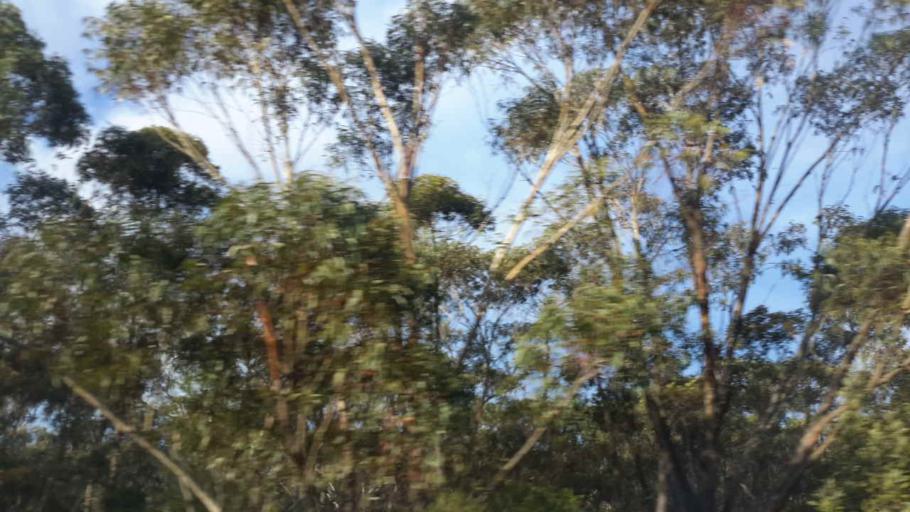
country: AU
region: New South Wales
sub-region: Wollongong
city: Bulli
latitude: -34.2477
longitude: 150.8489
